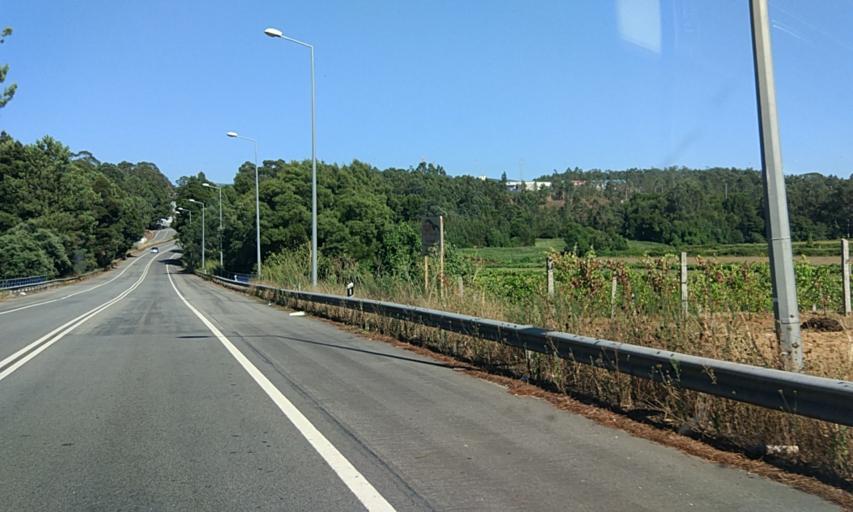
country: PT
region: Braga
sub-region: Vila Nova de Famalicao
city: Ferreiros
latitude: 41.3396
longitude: -8.5166
